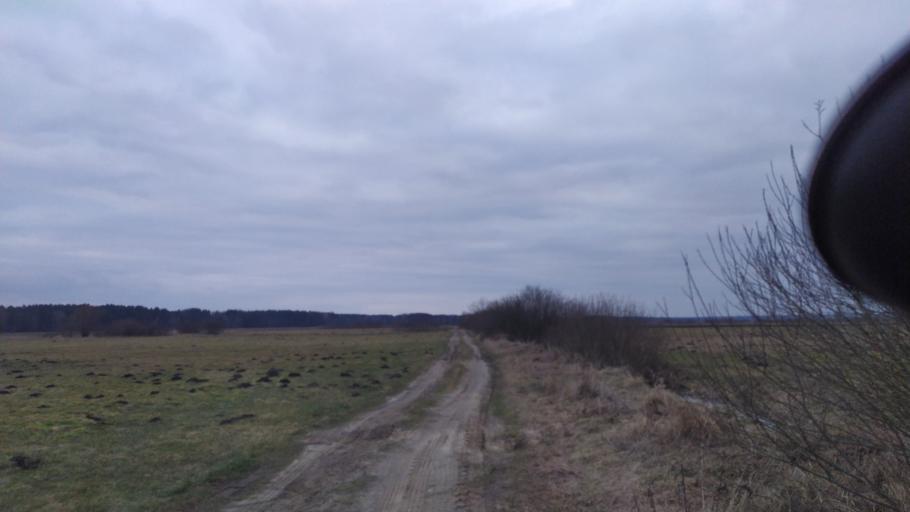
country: PL
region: Lublin Voivodeship
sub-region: Powiat lubartowski
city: Abramow
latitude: 51.4308
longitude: 22.3196
